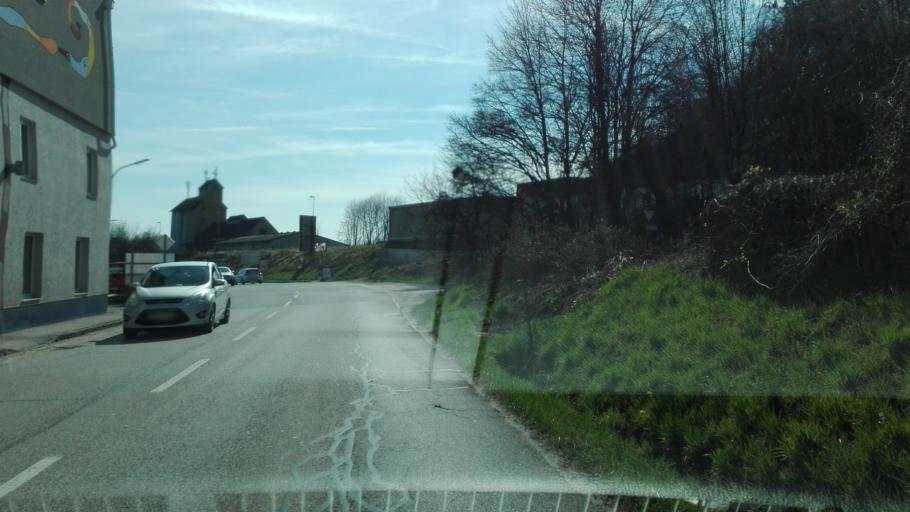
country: AT
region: Lower Austria
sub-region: Politischer Bezirk Amstetten
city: Ennsdorf
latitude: 48.2434
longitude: 14.5337
